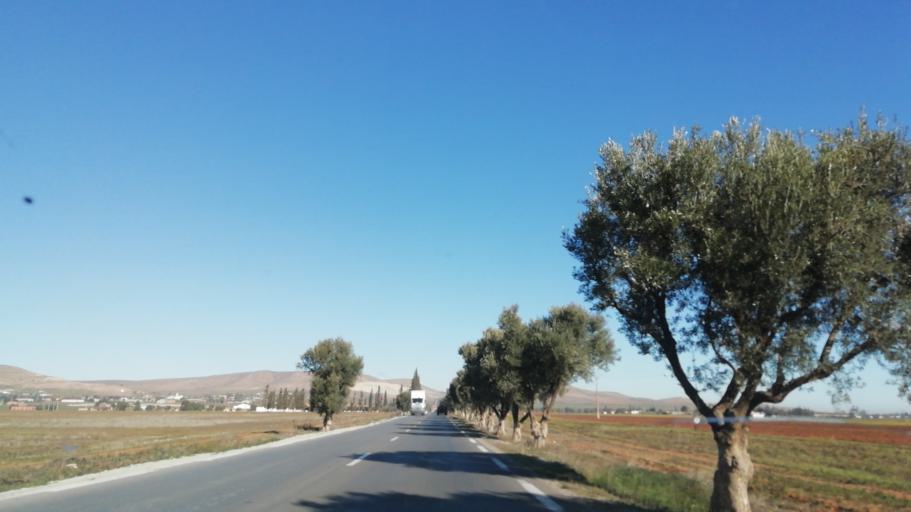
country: DZ
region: Mascara
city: Mascara
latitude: 35.2099
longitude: 0.1107
